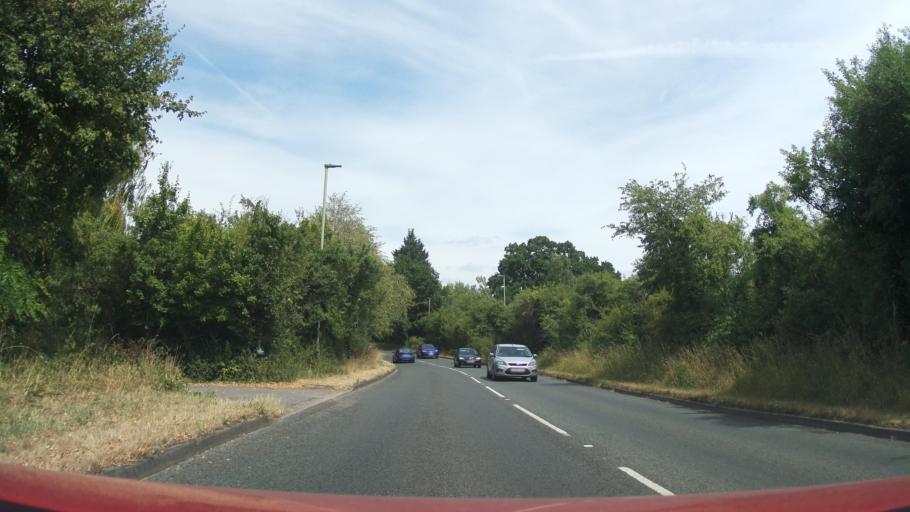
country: GB
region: England
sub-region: Surrey
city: Chilworth
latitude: 51.2505
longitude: -0.5262
